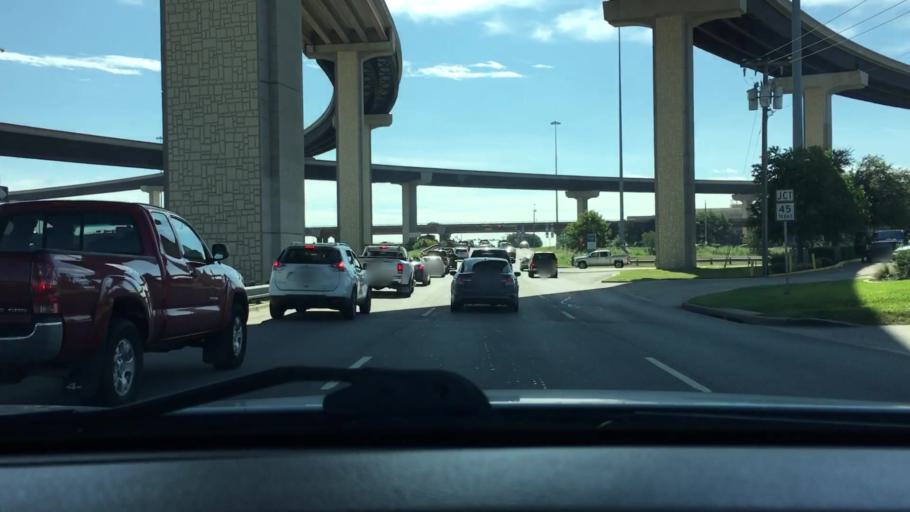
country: US
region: Texas
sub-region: Williamson County
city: Round Rock
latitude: 30.4829
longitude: -97.6753
